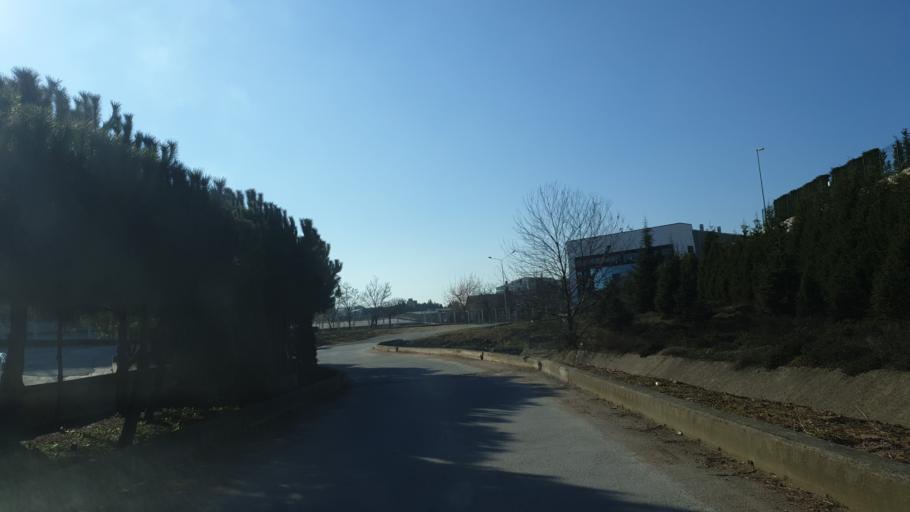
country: TR
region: Kocaeli
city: Balcik
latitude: 40.8776
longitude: 29.3724
